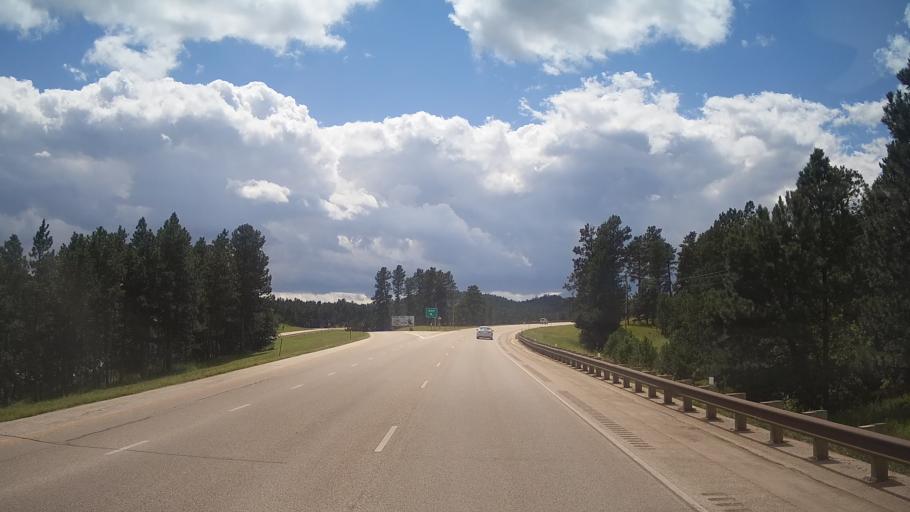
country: US
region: South Dakota
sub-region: Pennington County
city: Colonial Pine Hills
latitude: 43.9637
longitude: -103.3532
